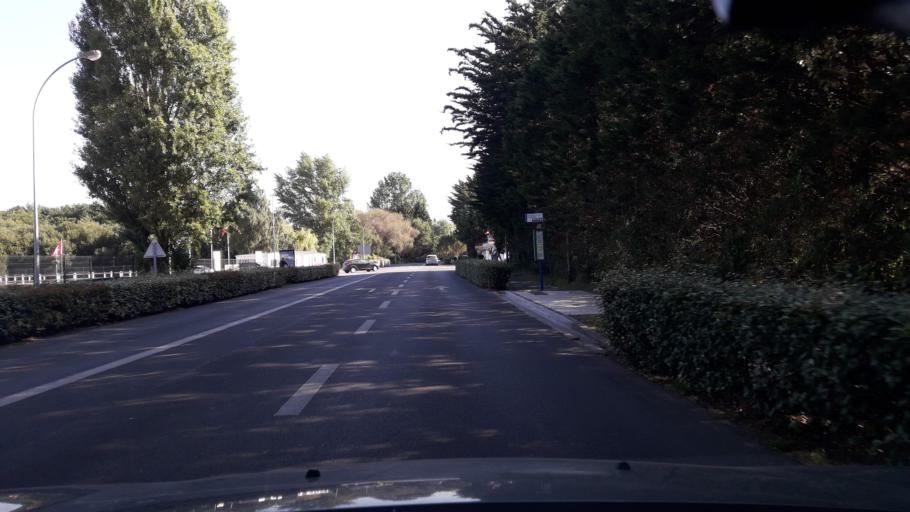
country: FR
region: Poitou-Charentes
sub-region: Departement de la Charente-Maritime
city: Les Mathes
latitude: 45.7133
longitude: -1.1598
